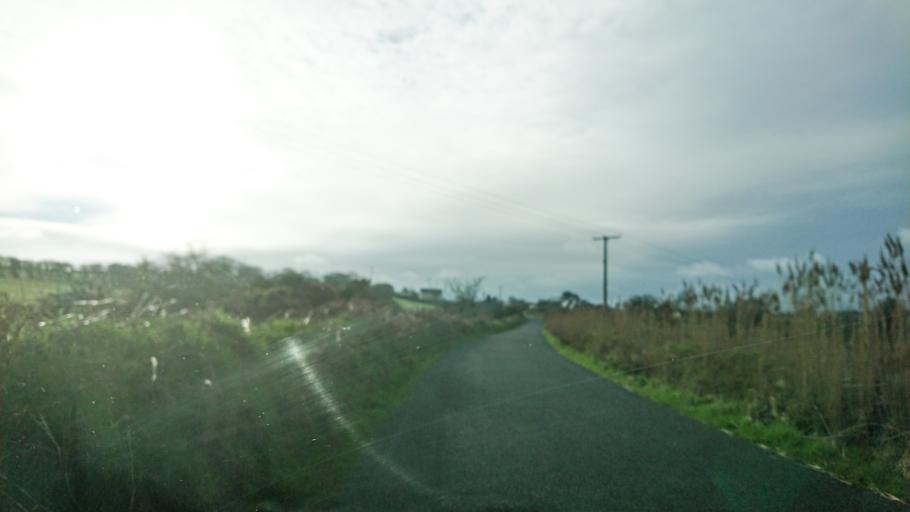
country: IE
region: Munster
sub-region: Waterford
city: Tra Mhor
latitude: 52.1588
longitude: -7.1887
